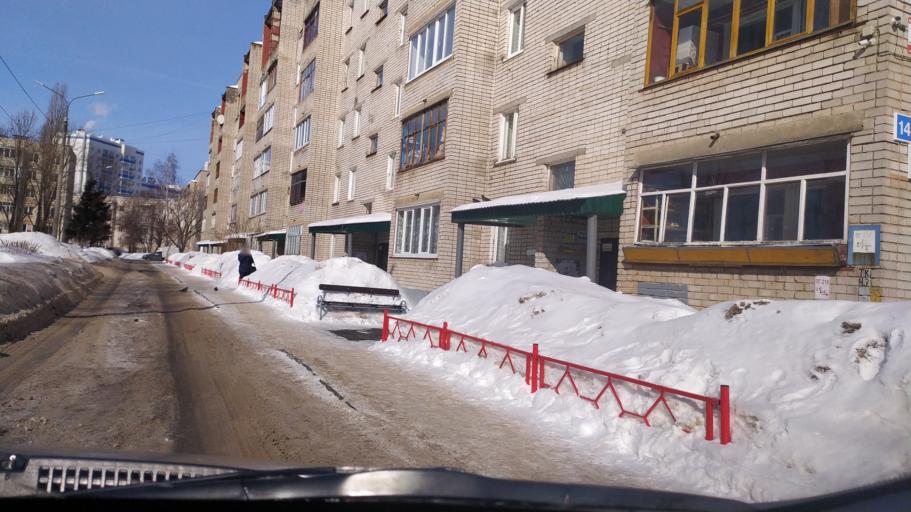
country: RU
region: Chuvashia
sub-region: Cheboksarskiy Rayon
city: Cheboksary
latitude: 56.1498
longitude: 47.2231
